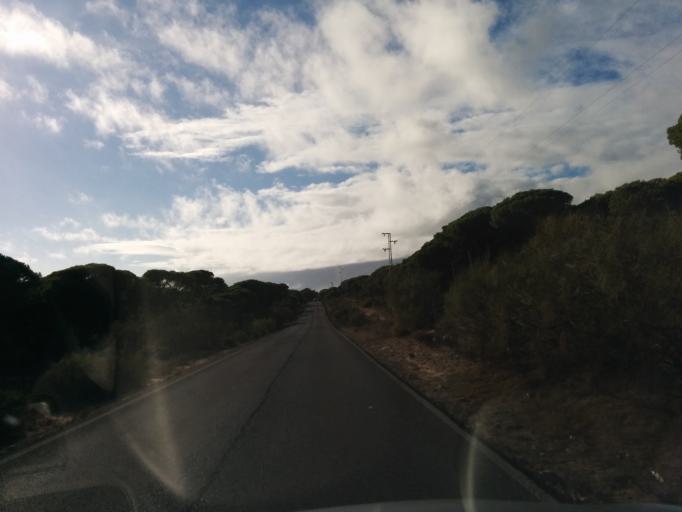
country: ES
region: Andalusia
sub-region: Provincia de Cadiz
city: Vejer de la Frontera
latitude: 36.1928
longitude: -5.9878
